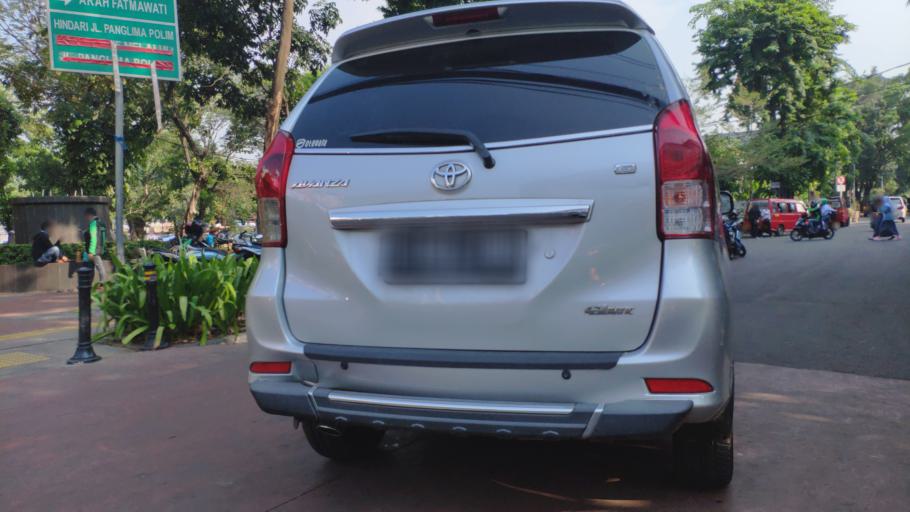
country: ID
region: Jakarta Raya
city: Jakarta
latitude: -6.2460
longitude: 106.8000
